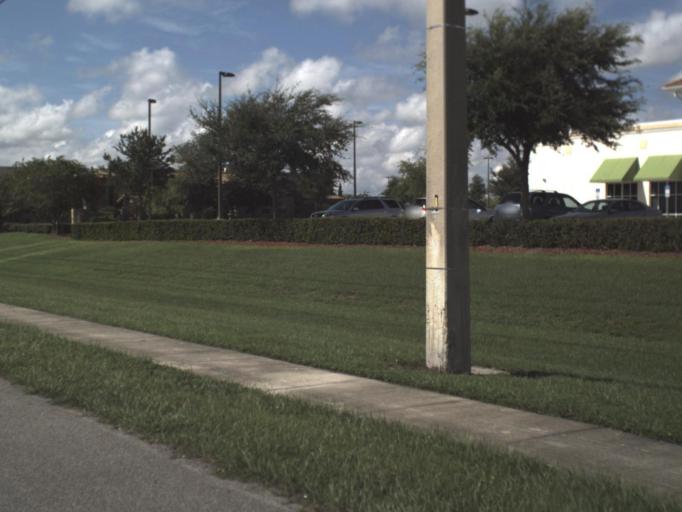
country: US
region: Florida
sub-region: Polk County
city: Medulla
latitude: 28.0021
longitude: -81.9752
